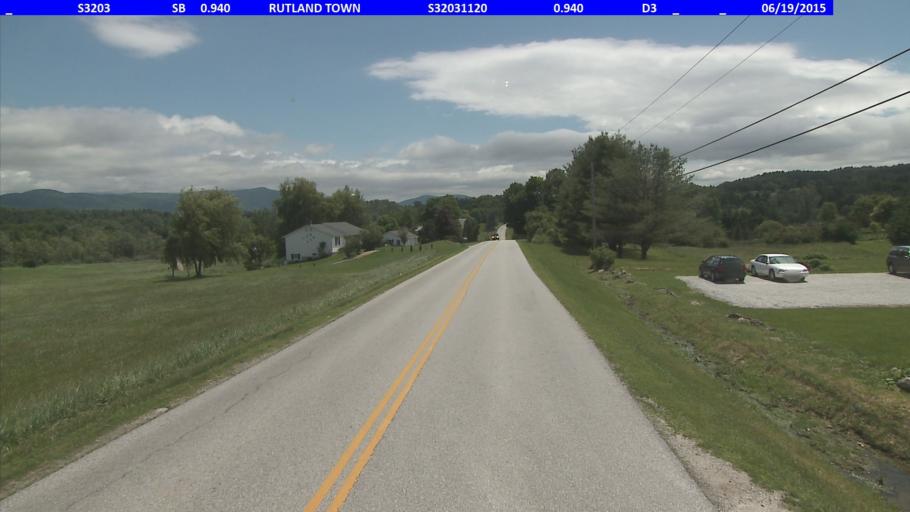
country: US
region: Vermont
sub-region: Rutland County
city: Rutland
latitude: 43.6660
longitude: -73.0024
